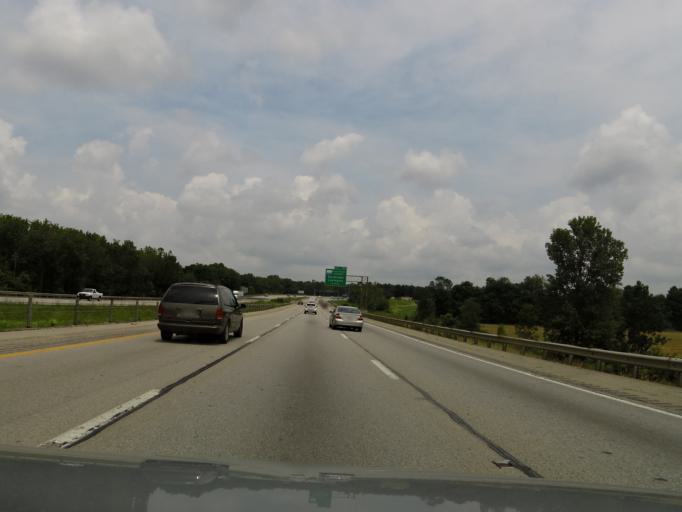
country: US
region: Kentucky
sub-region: Hardin County
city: Elizabethtown
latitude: 37.6852
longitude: -85.8425
